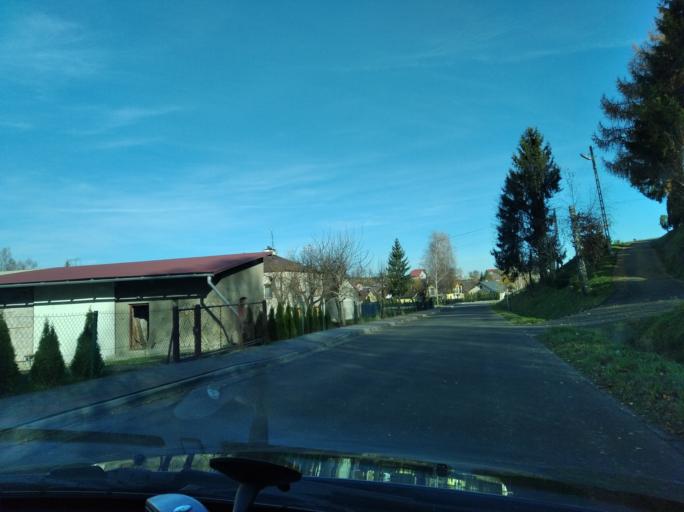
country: PL
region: Subcarpathian Voivodeship
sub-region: Powiat rzeszowski
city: Lutoryz
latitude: 49.9643
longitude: 21.8974
